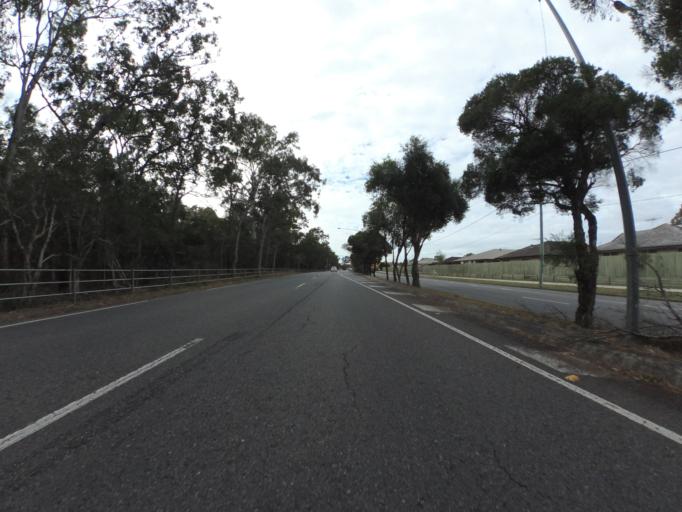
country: AU
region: Queensland
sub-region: Brisbane
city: Wynnum West
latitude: -27.4675
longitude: 153.1390
